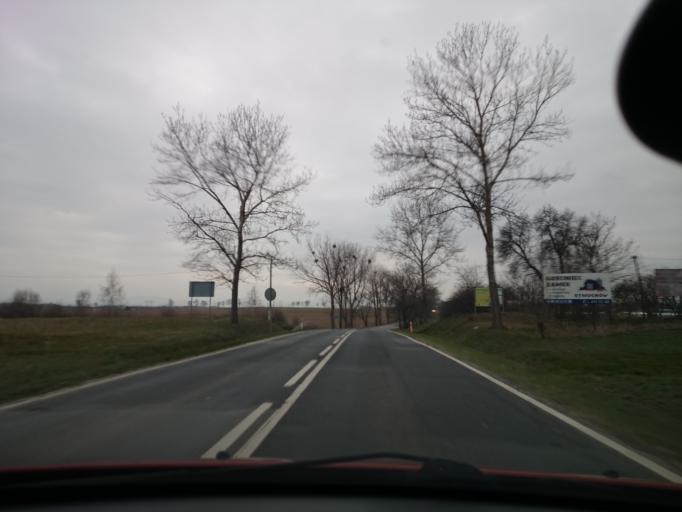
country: PL
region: Opole Voivodeship
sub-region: Powiat nyski
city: Nysa
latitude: 50.4768
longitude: 17.2731
